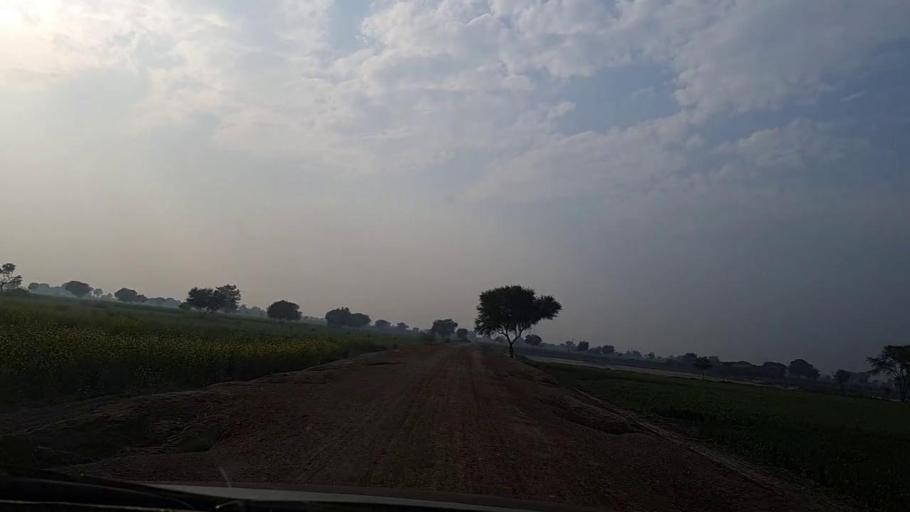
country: PK
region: Sindh
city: Nawabshah
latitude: 26.2739
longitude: 68.3296
